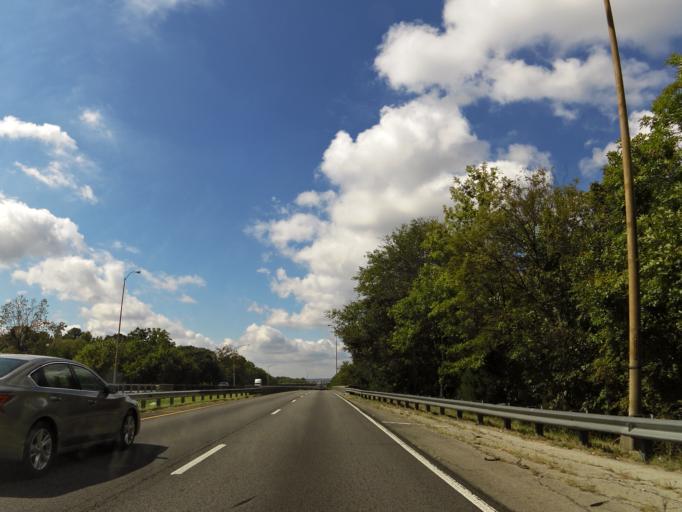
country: US
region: Alabama
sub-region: Jefferson County
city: Fairfield
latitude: 33.4773
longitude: -86.9248
